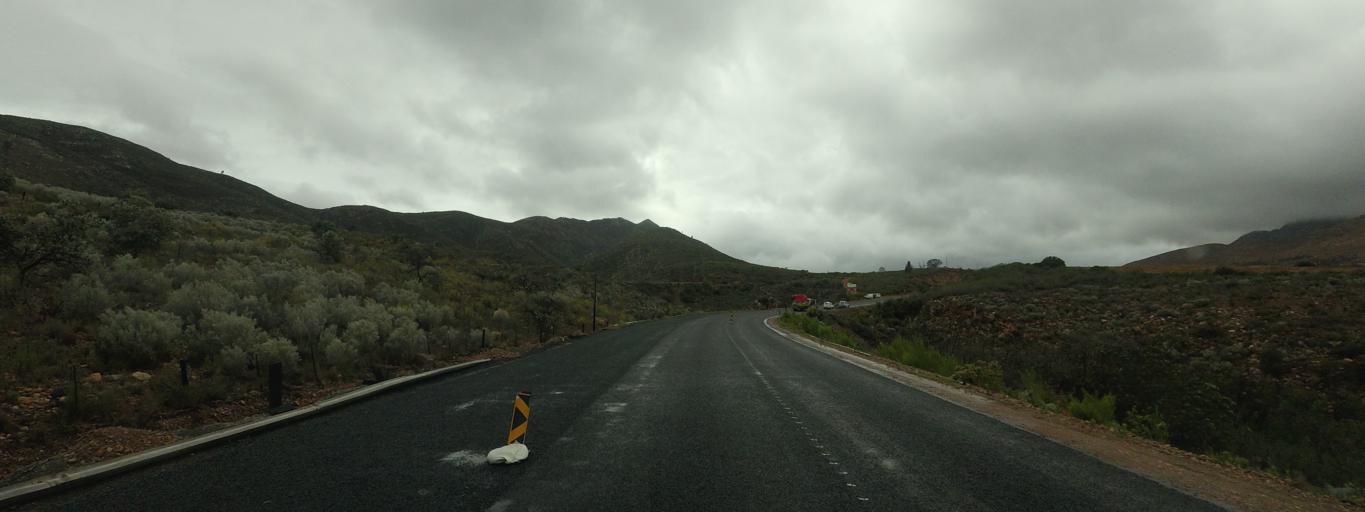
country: ZA
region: Western Cape
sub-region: Eden District Municipality
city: George
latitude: -33.8116
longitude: 22.3444
